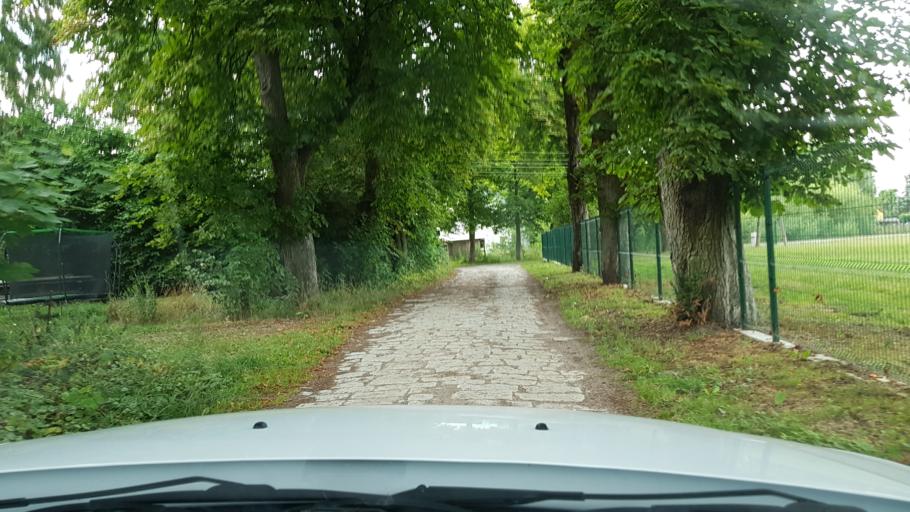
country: PL
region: West Pomeranian Voivodeship
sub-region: Powiat swidwinski
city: Polczyn-Zdroj
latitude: 53.8022
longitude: 16.0752
